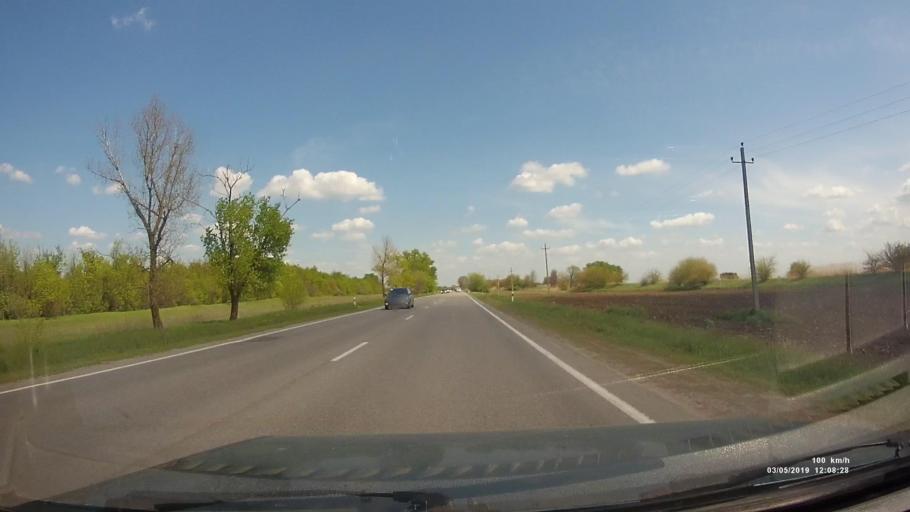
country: RU
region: Rostov
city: Bagayevskaya
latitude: 47.2877
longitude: 40.4961
